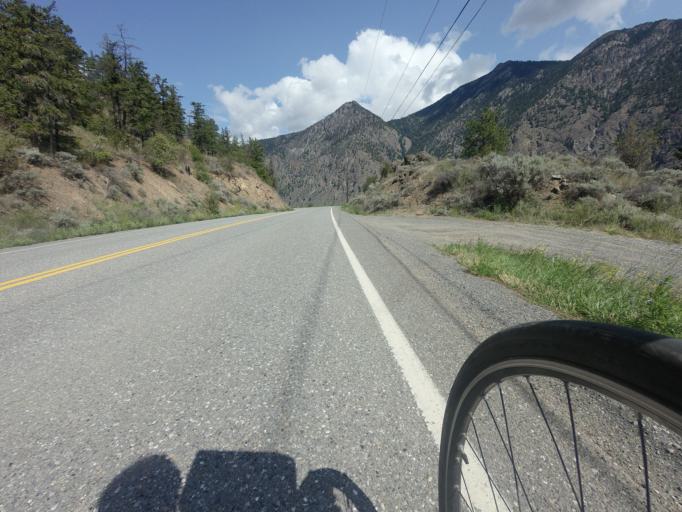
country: CA
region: British Columbia
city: Lillooet
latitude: 50.7546
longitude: -121.8953
